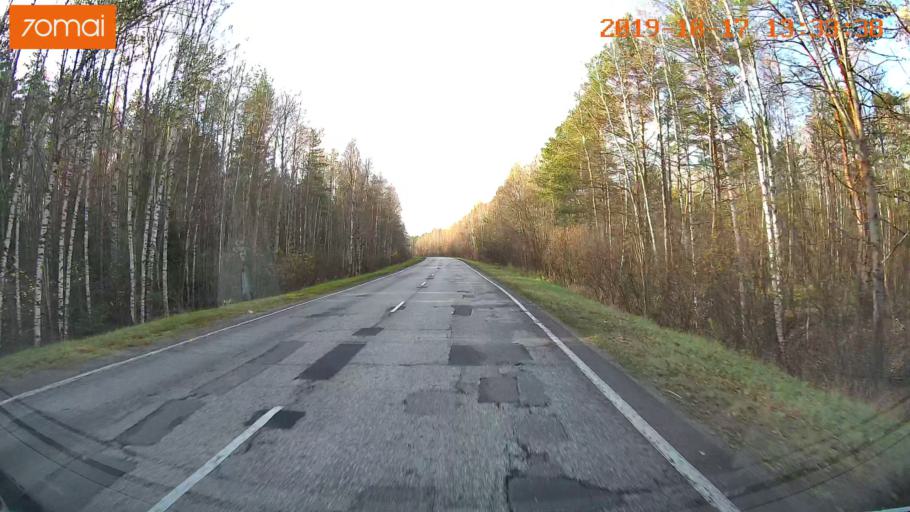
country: RU
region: Vladimir
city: Velikodvorskiy
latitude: 55.1436
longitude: 40.7368
